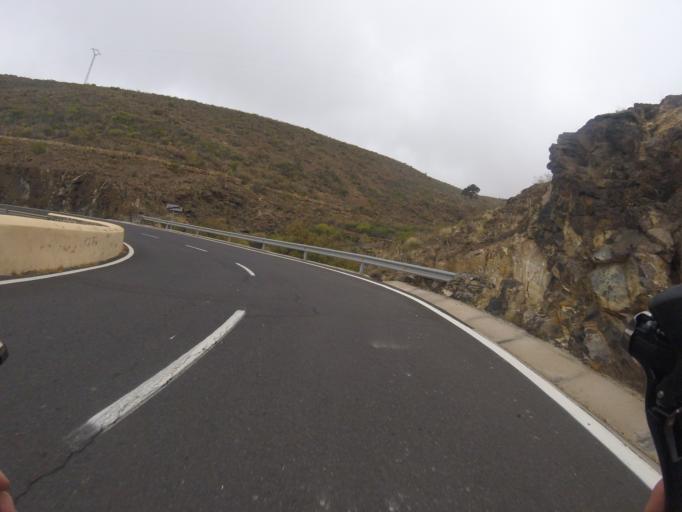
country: ES
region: Canary Islands
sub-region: Provincia de Santa Cruz de Tenerife
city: Fasnia
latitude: 28.2104
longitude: -16.4543
